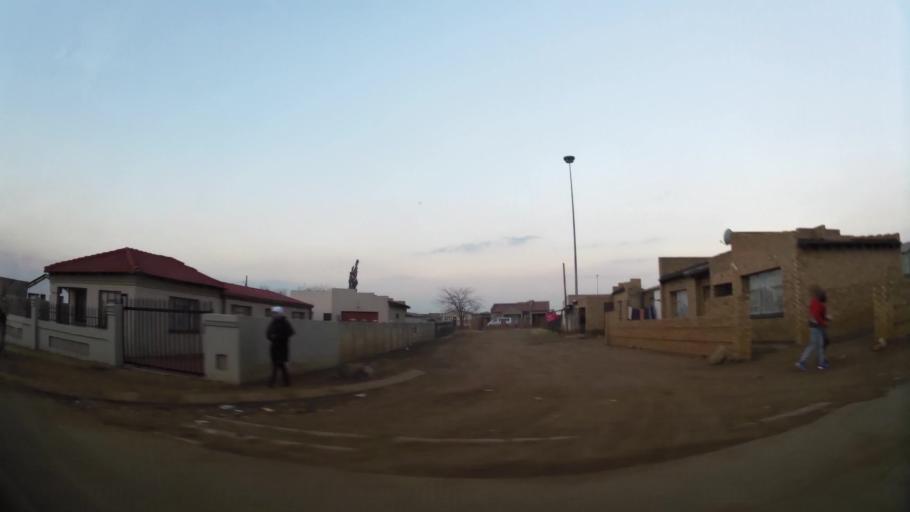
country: ZA
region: Gauteng
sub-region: City of Johannesburg Metropolitan Municipality
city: Orange Farm
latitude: -26.5513
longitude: 27.8597
